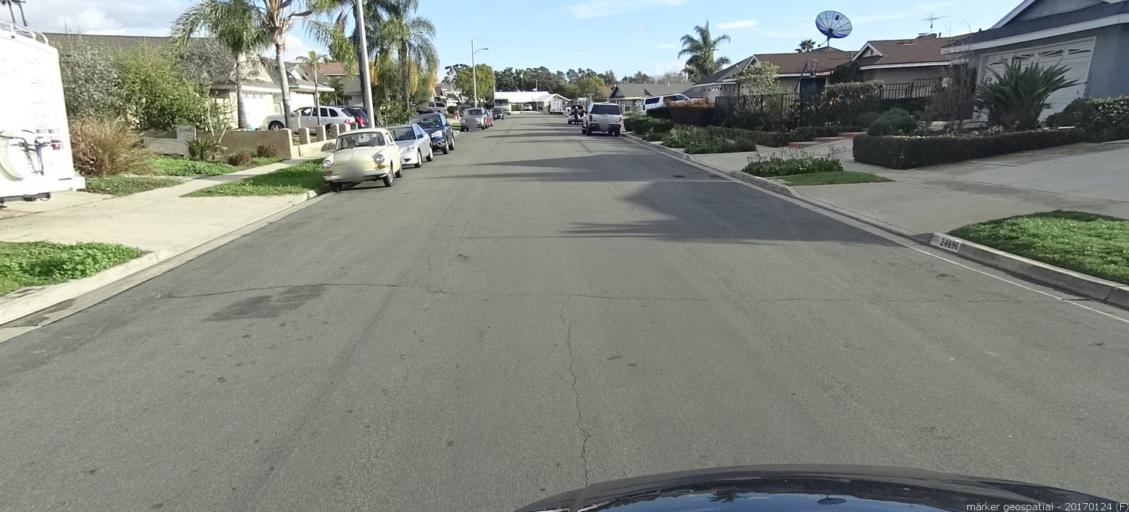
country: US
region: California
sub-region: Orange County
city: Lake Forest
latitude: 33.6303
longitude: -117.6987
